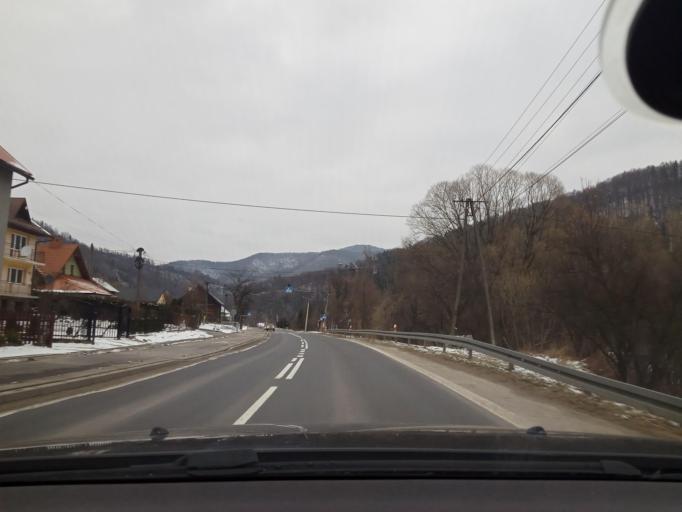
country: PL
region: Lesser Poland Voivodeship
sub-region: Powiat nowotarski
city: Kroscienko nad Dunajcem
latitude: 49.4590
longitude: 20.4269
